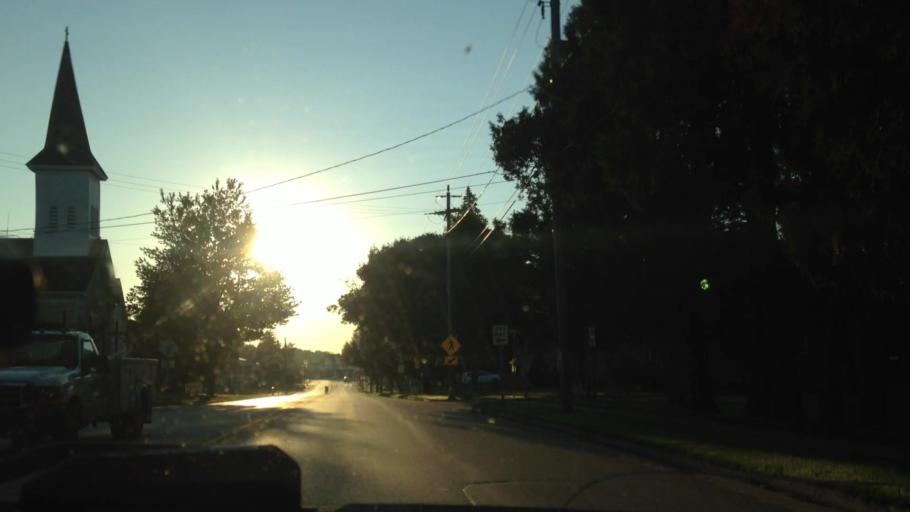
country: US
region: Wisconsin
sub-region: Ozaukee County
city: Saukville
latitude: 43.3821
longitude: -87.9437
